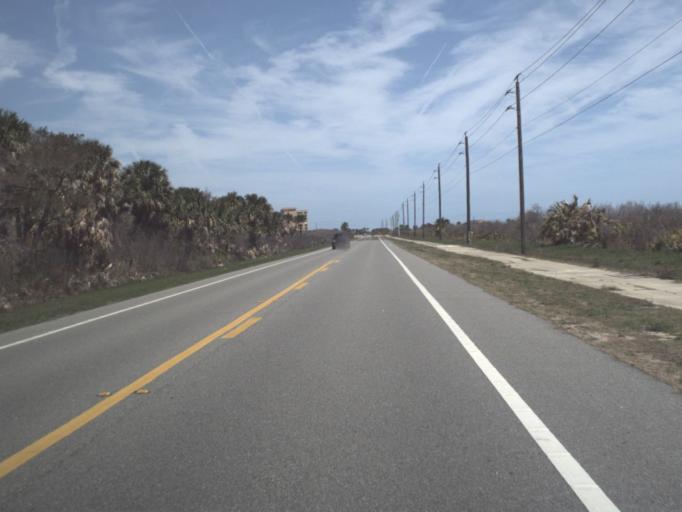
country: US
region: Florida
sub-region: Flagler County
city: Palm Coast
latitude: 29.6373
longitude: -81.2041
